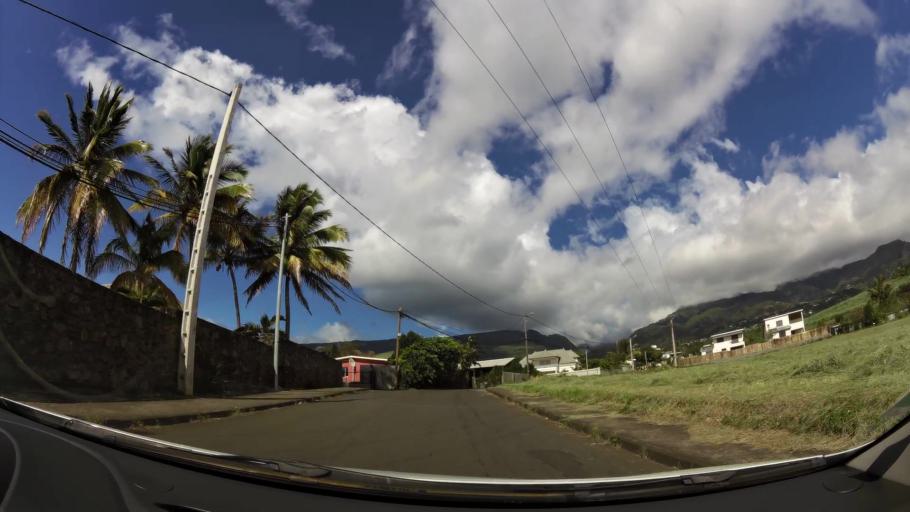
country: RE
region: Reunion
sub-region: Reunion
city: Sainte-Marie
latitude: -20.9197
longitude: 55.5010
